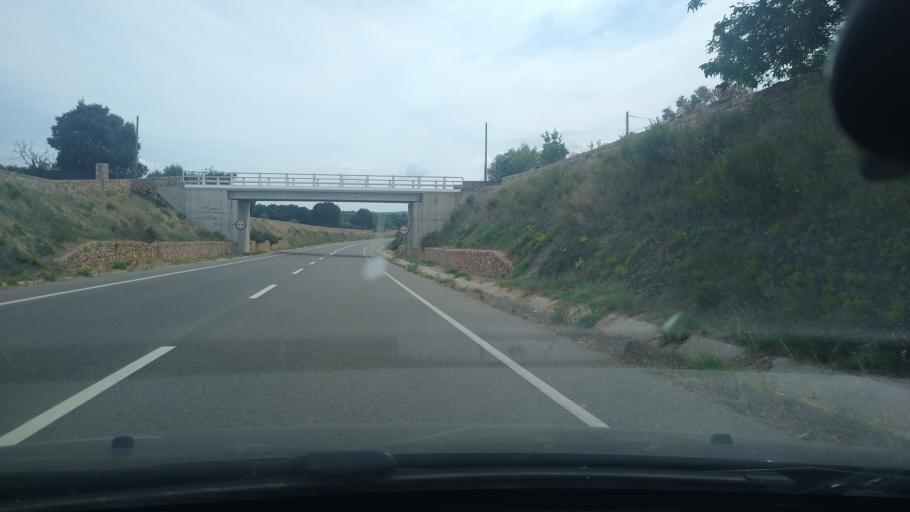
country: ES
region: Balearic Islands
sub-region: Illes Balears
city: Llubi
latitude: 39.6978
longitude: 3.0129
